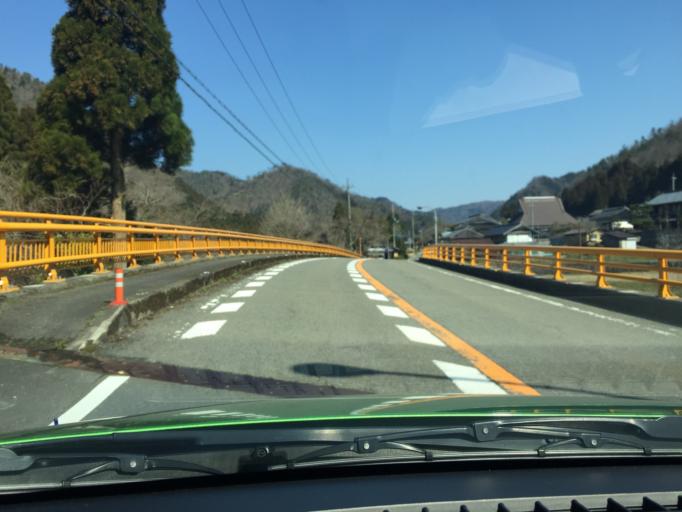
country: JP
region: Kyoto
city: Maizuru
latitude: 35.2935
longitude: 135.5571
